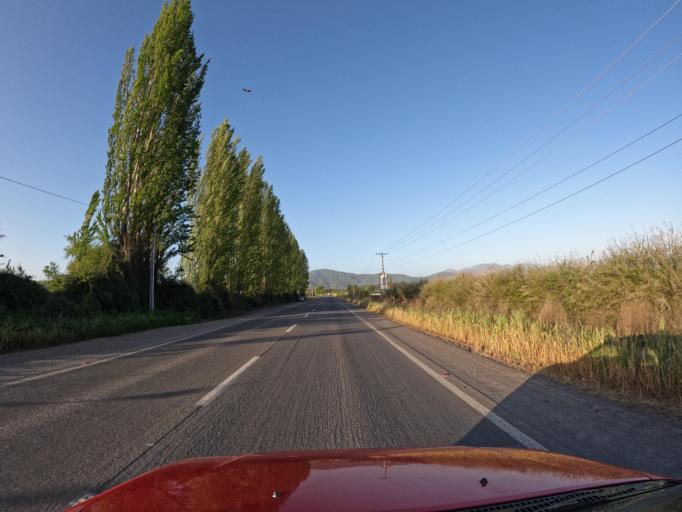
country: CL
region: O'Higgins
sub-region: Provincia de Cachapoal
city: San Vicente
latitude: -34.2966
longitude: -71.3714
